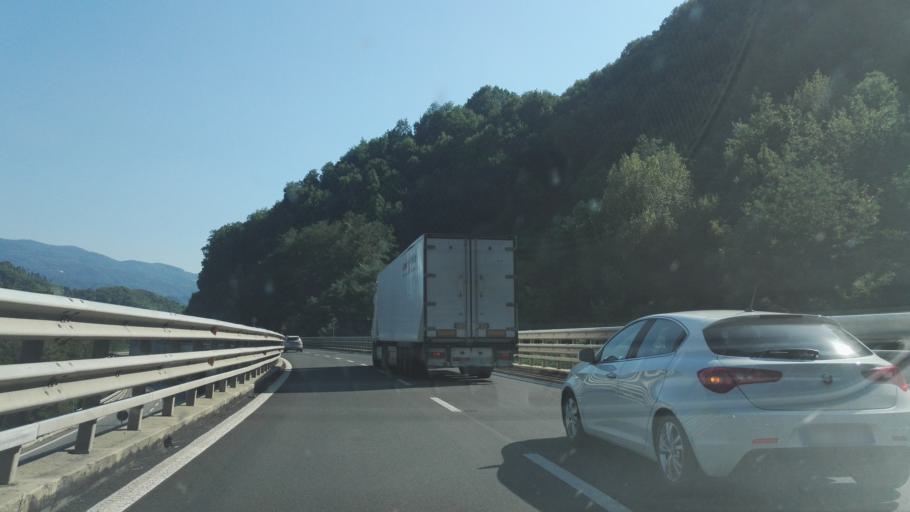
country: IT
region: Calabria
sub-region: Provincia di Cosenza
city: Altilia
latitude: 39.1429
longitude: 16.2745
